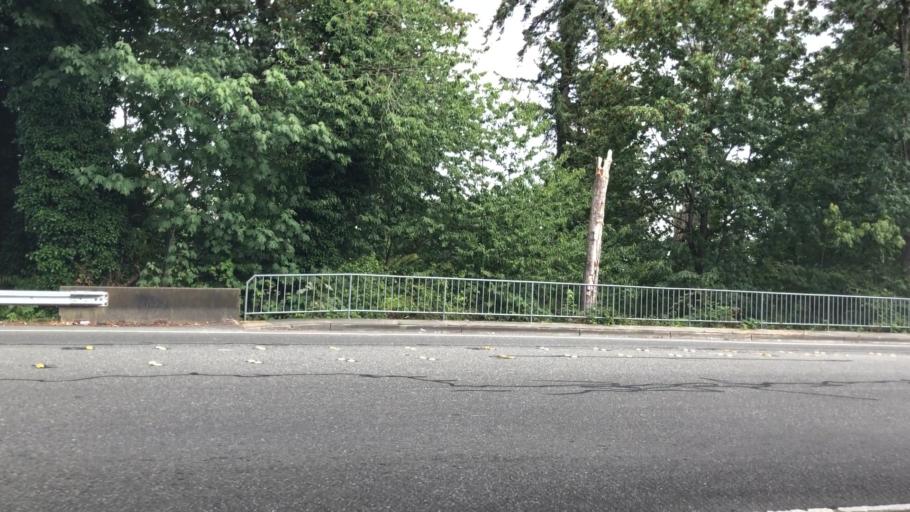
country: US
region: Washington
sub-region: Snohomish County
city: Alderwood Manor
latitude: 47.8510
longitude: -122.2820
